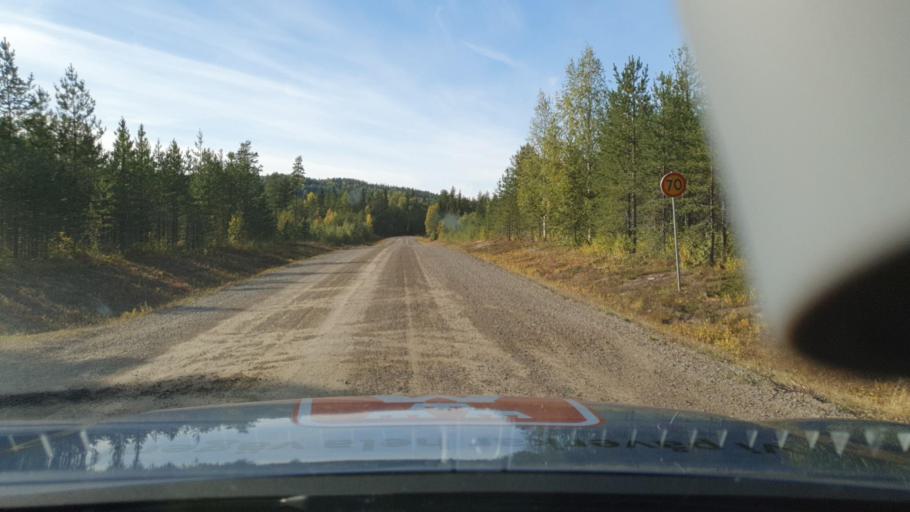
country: SE
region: Norrbotten
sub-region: Alvsbyns Kommun
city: AElvsbyn
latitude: 66.1399
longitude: 20.5471
